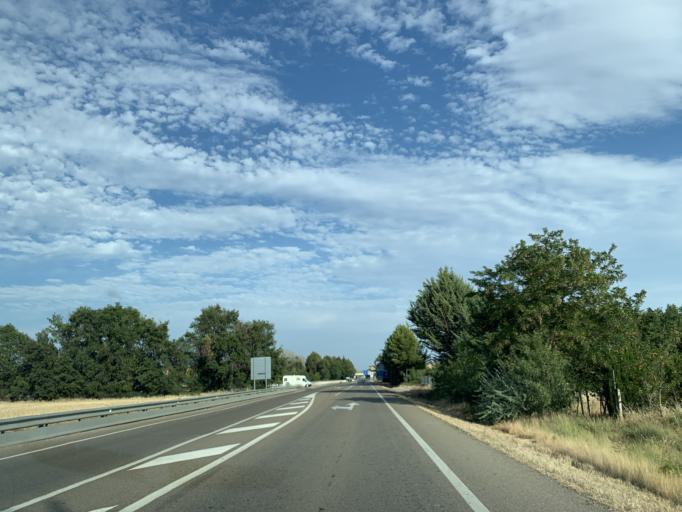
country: ES
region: Aragon
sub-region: Provincia de Huesca
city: Chimillas
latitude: 42.1512
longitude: -0.4319
